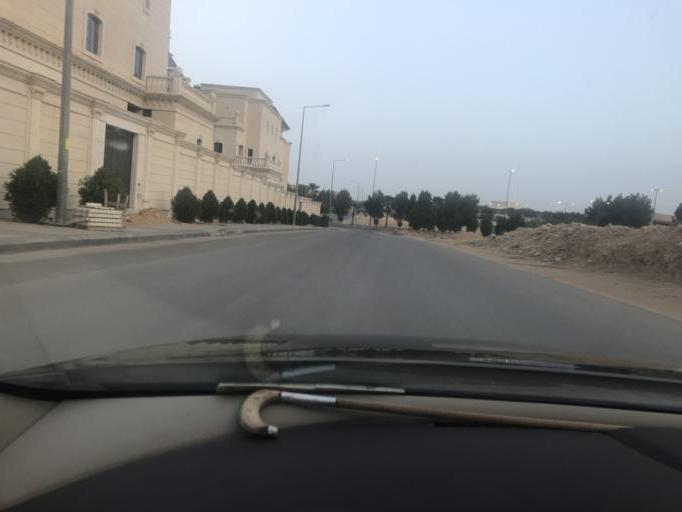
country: SA
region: Ar Riyad
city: Riyadh
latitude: 24.7261
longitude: 46.7494
